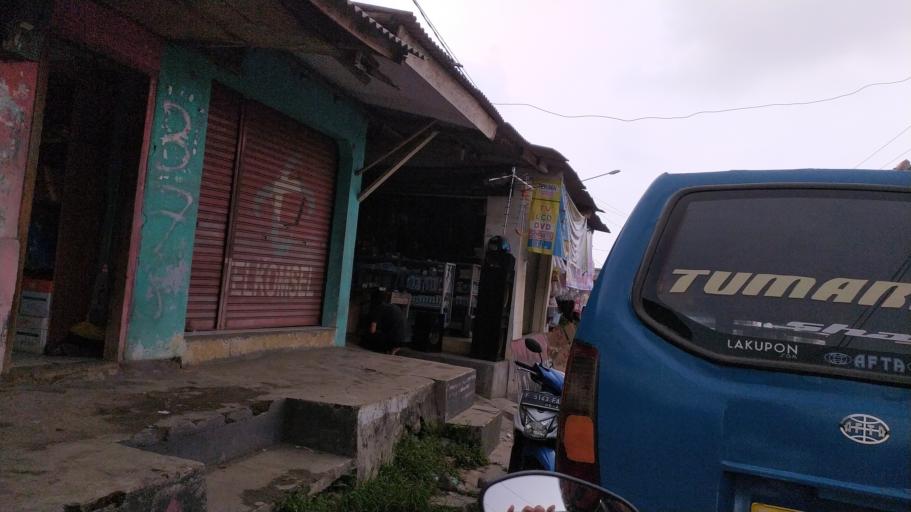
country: ID
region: West Java
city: Ciampea
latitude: -6.6192
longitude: 106.6953
